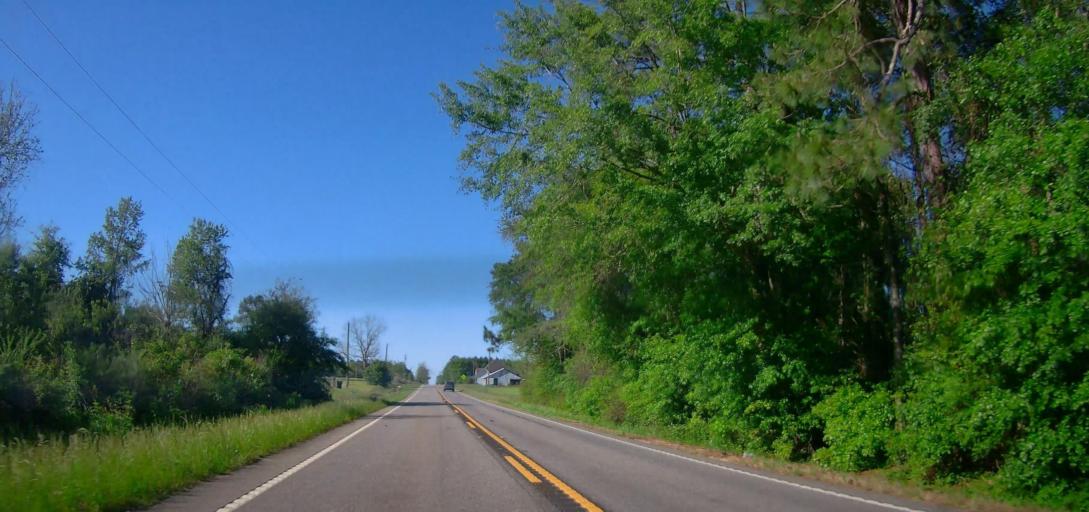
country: US
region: Georgia
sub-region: Wilcox County
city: Rochelle
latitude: 31.8195
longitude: -83.4891
